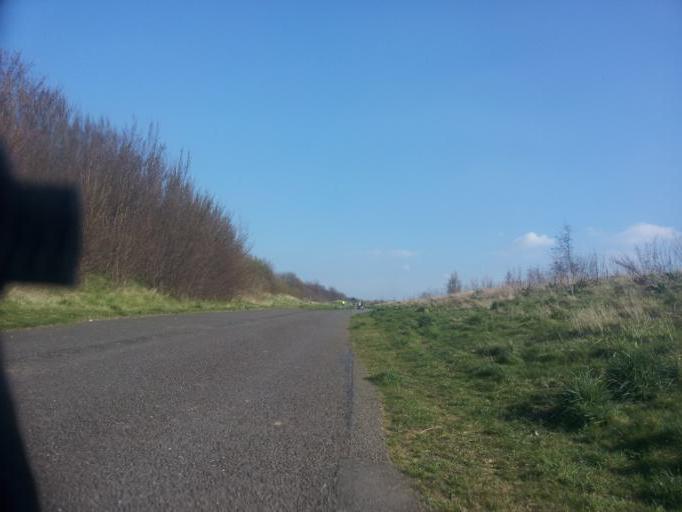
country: GB
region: England
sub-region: Kent
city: Gravesend
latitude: 51.4230
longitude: 0.3416
